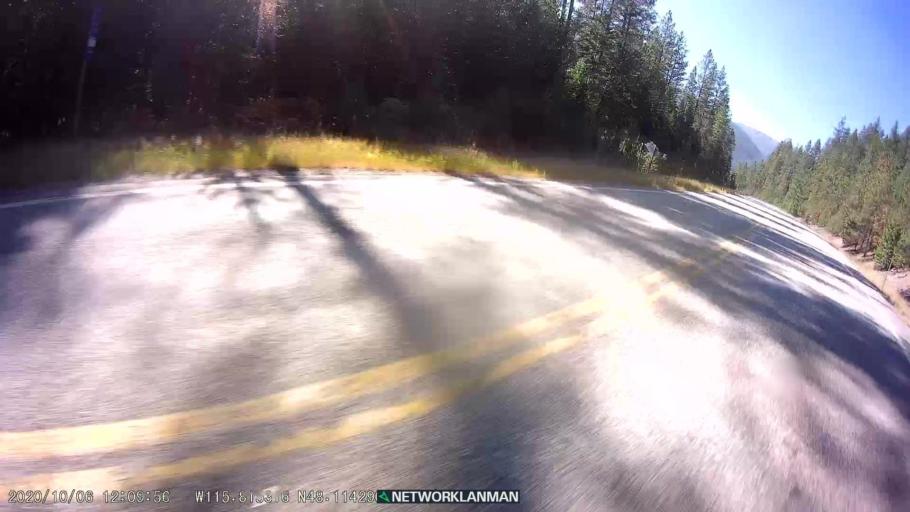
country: US
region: Montana
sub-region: Lincoln County
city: Libby
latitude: 48.1143
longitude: -115.8157
